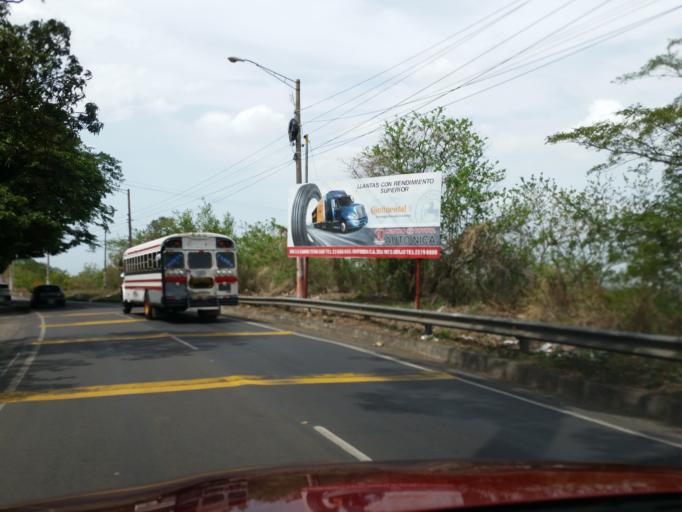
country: NI
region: Managua
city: Ciudad Sandino
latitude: 12.0958
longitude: -86.3235
